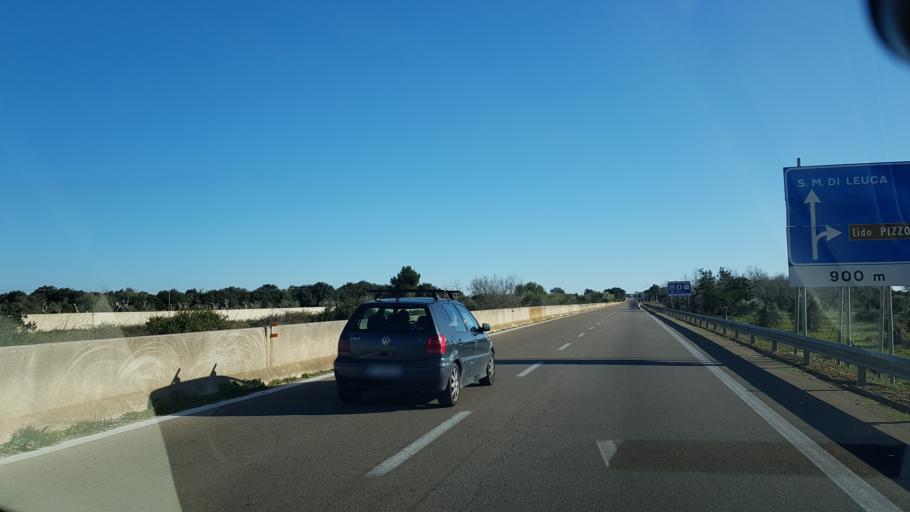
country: IT
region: Apulia
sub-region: Provincia di Lecce
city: Alezio
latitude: 40.0203
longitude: 18.0420
